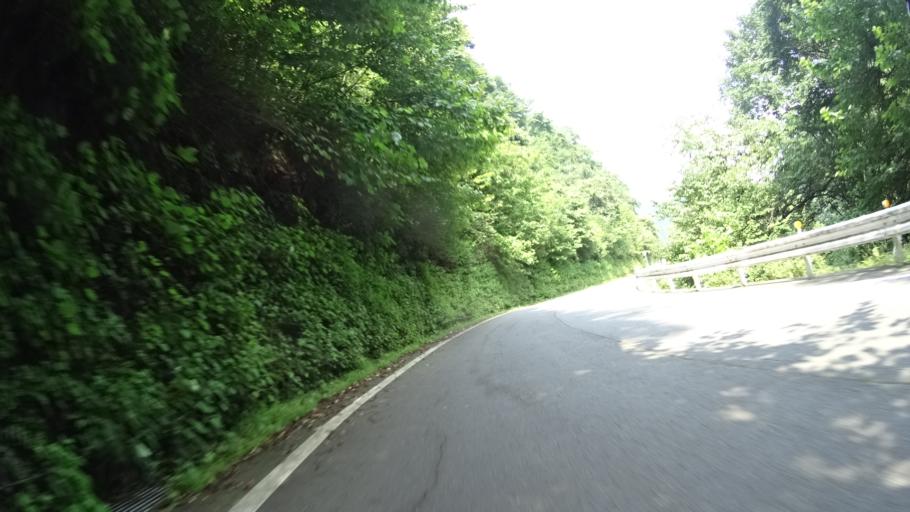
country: JP
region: Gunma
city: Tomioka
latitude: 36.0604
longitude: 138.8376
